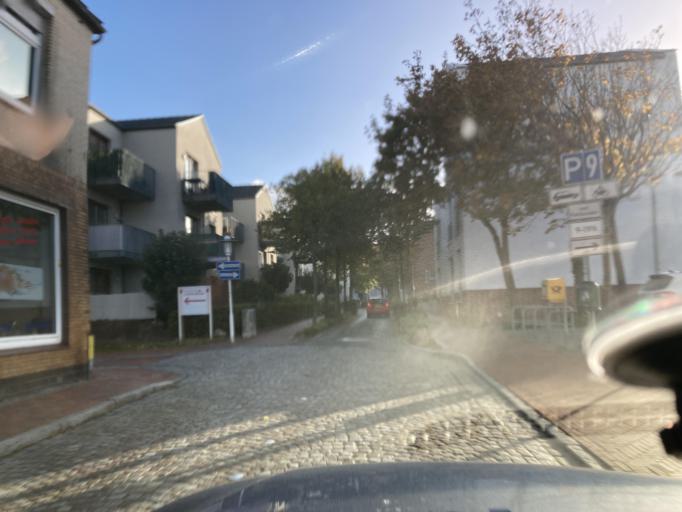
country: DE
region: Schleswig-Holstein
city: Busum
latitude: 54.1306
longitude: 8.8620
